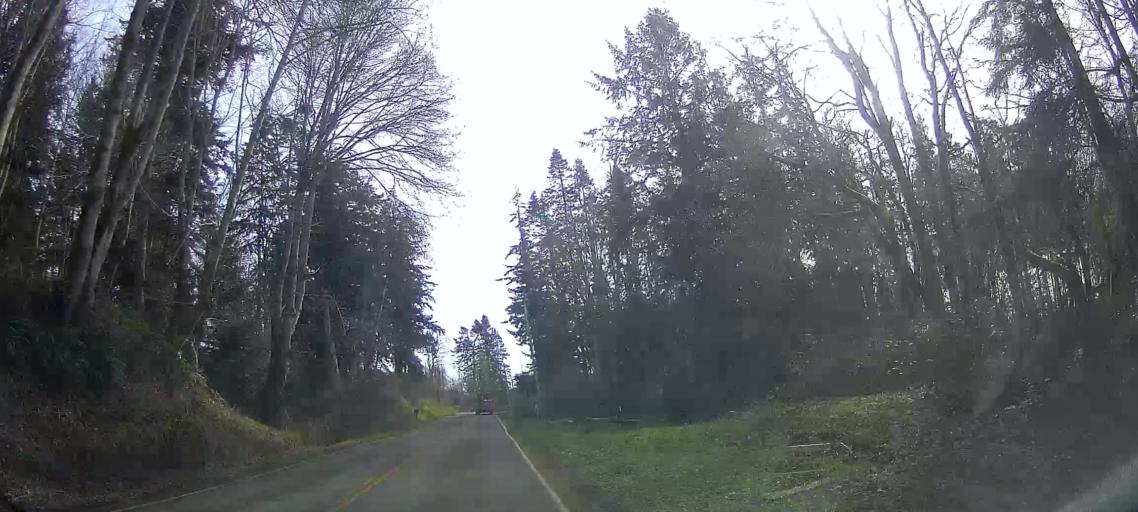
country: US
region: Washington
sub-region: Island County
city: Langley
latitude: 48.0751
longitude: -122.3888
